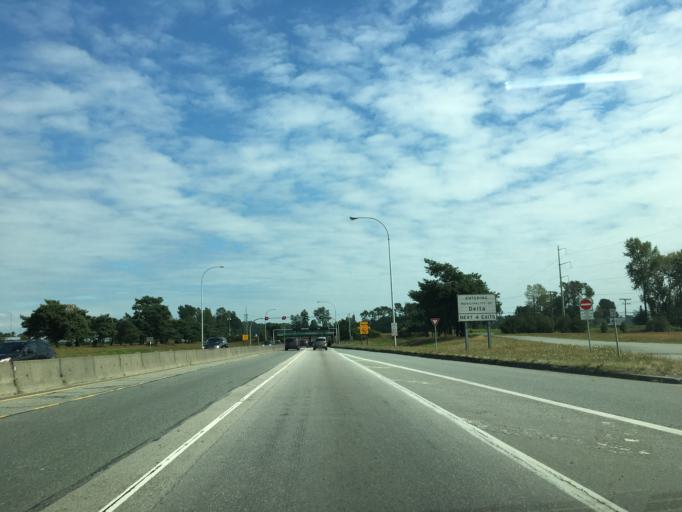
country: CA
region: British Columbia
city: Ladner
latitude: 49.1278
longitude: -123.0831
